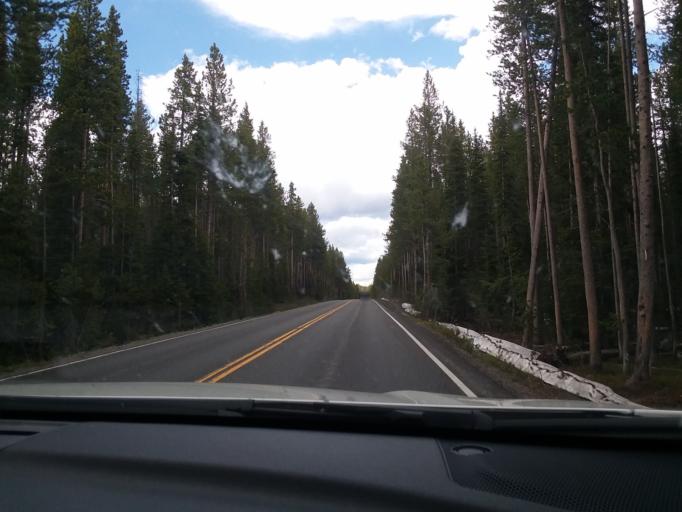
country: US
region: Idaho
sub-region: Teton County
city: Driggs
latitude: 44.1738
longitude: -110.6620
